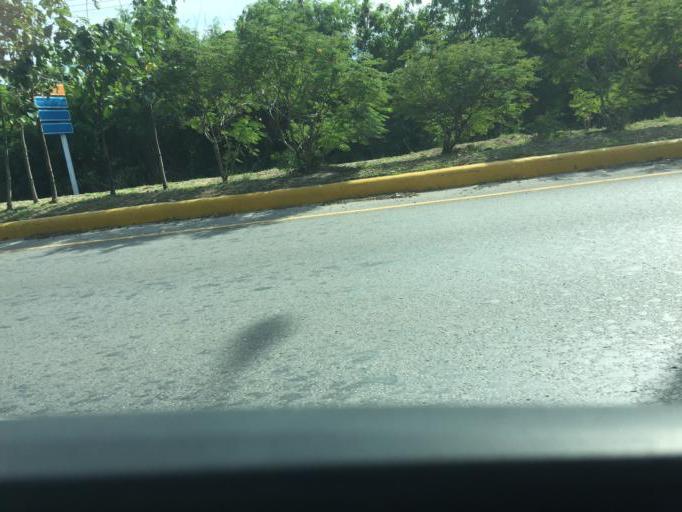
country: DO
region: San Juan
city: Punta Cana
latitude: 18.5600
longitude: -68.3748
